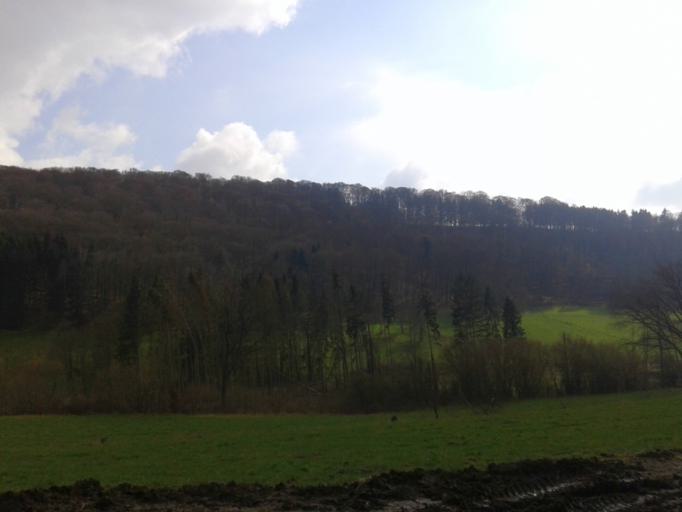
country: LU
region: Luxembourg
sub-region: Canton de Mersch
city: Tuntange
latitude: 49.6988
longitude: 6.0130
